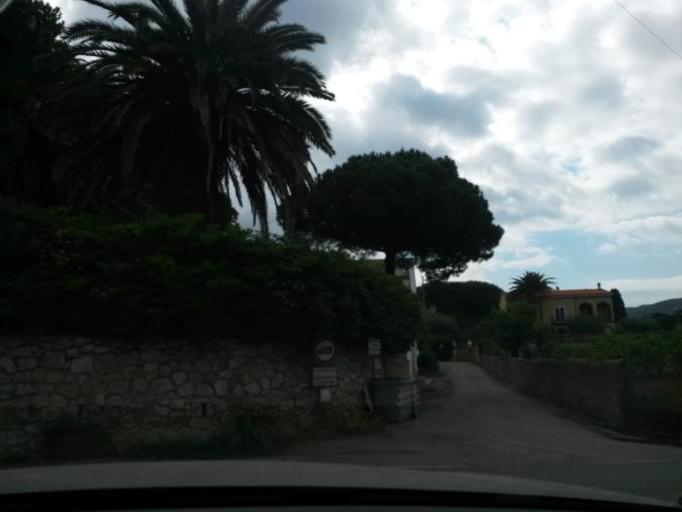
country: IT
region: Tuscany
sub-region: Provincia di Livorno
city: Rio nell'Elba
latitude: 42.7984
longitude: 10.3598
